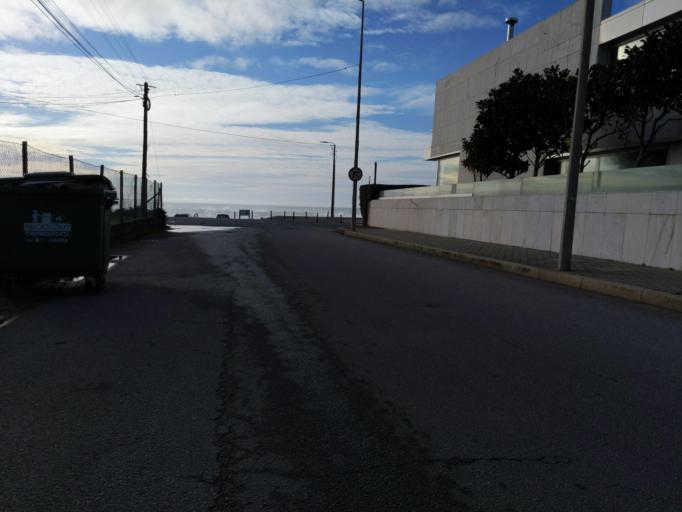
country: PT
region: Porto
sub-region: Vila Nova de Gaia
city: Arcozelo
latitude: 41.0448
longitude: -8.6509
